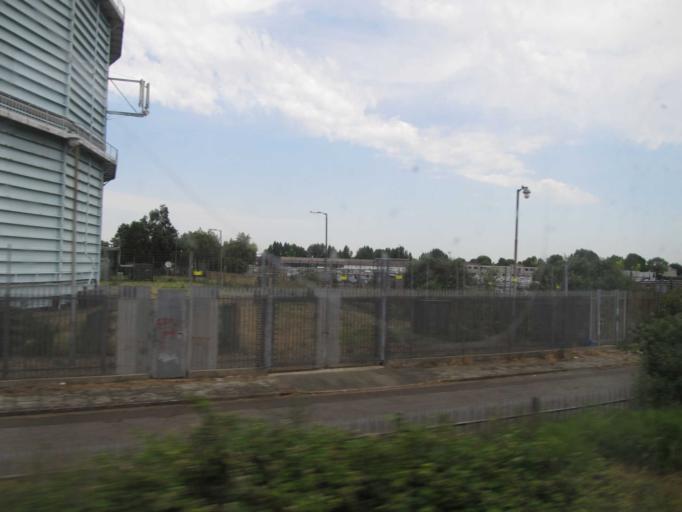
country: GB
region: England
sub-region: Greater London
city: Southall
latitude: 51.5045
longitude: -0.3895
